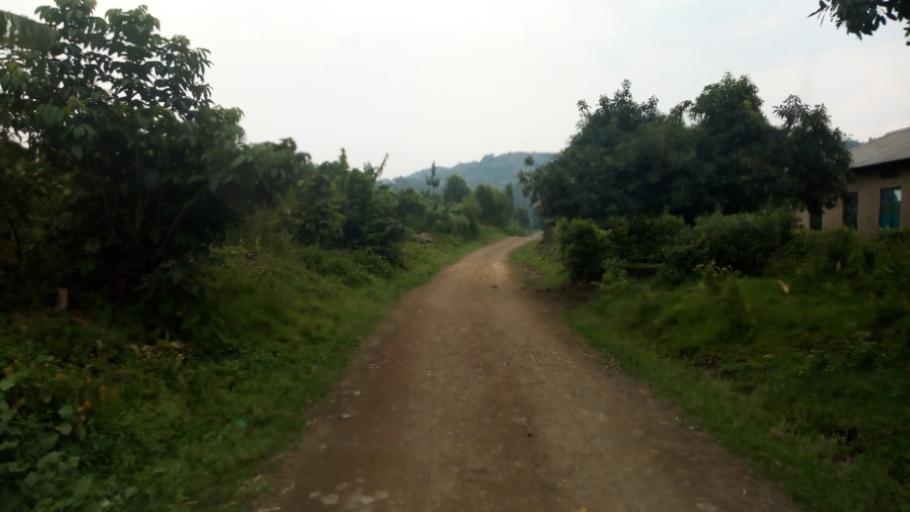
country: UG
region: Western Region
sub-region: Kisoro District
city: Kisoro
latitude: -1.2637
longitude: 29.6267
